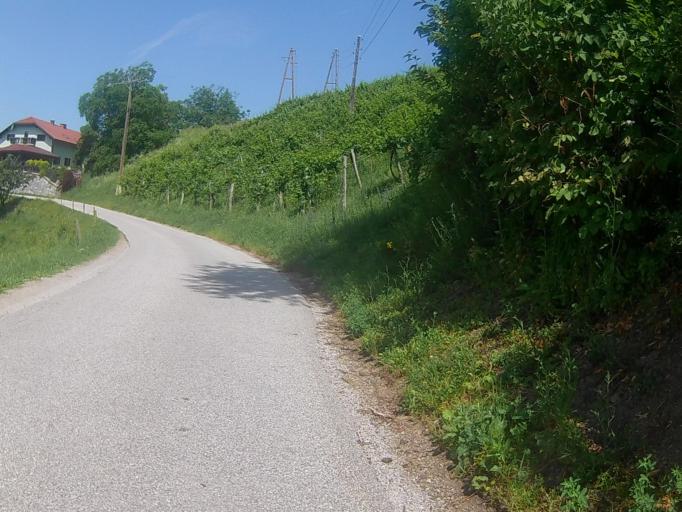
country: SI
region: Maribor
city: Kamnica
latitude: 46.6062
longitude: 15.6040
